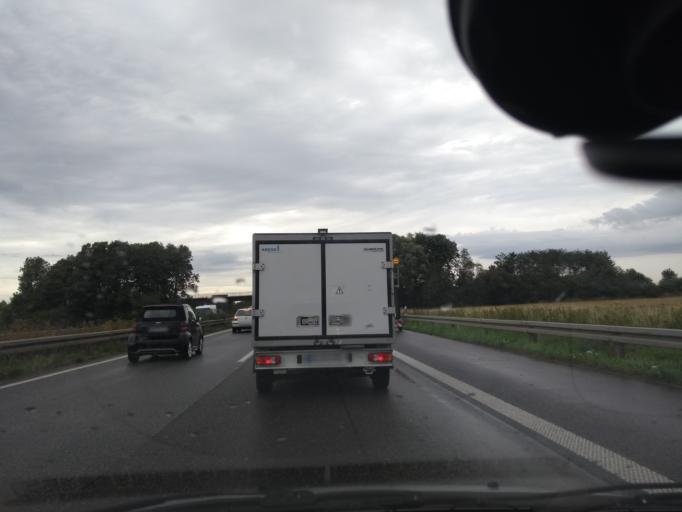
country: DE
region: North Rhine-Westphalia
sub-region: Regierungsbezirk Koln
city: Alsdorf
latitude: 50.8320
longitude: 6.1852
